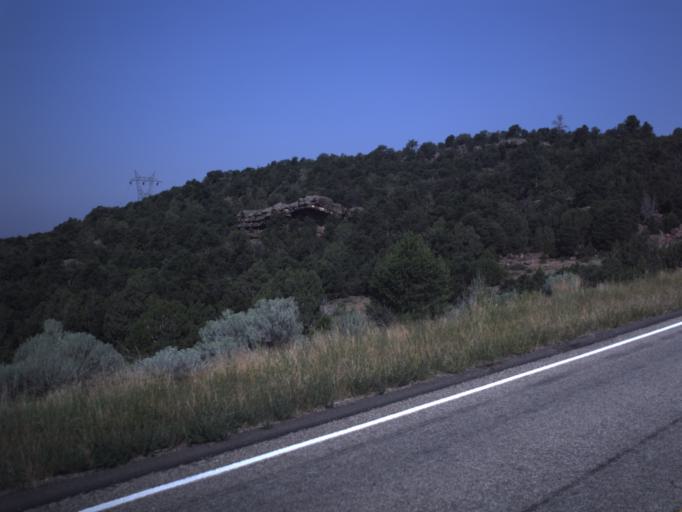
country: US
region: Utah
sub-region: Daggett County
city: Manila
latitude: 40.9142
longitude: -109.4131
